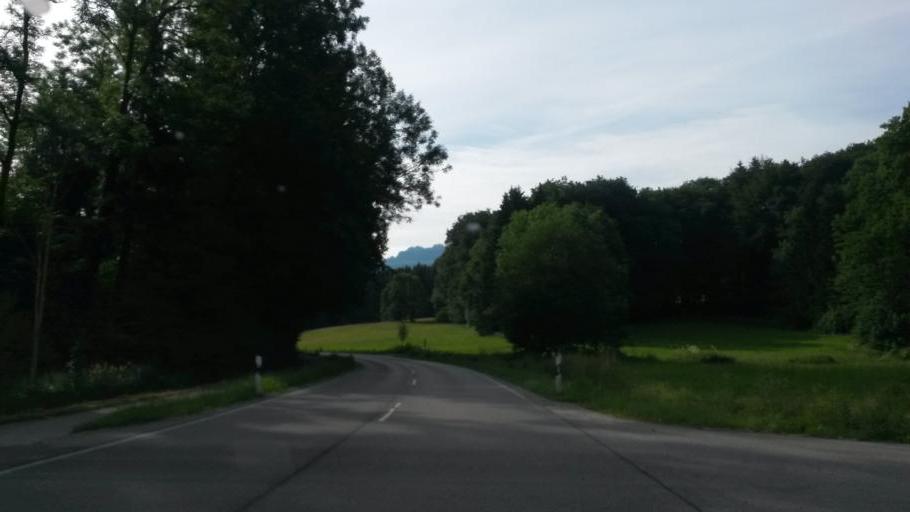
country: DE
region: Bavaria
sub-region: Upper Bavaria
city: Frasdorf
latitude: 47.7950
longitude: 12.2993
